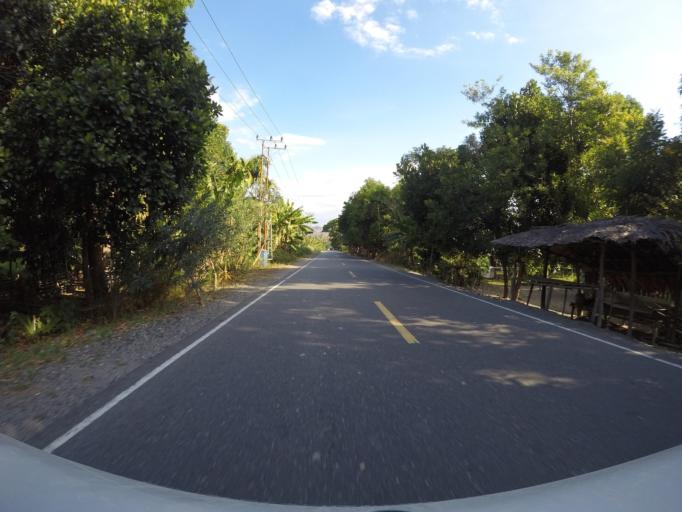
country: TL
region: Liquica
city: Maubara
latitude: -8.7343
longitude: 125.1363
